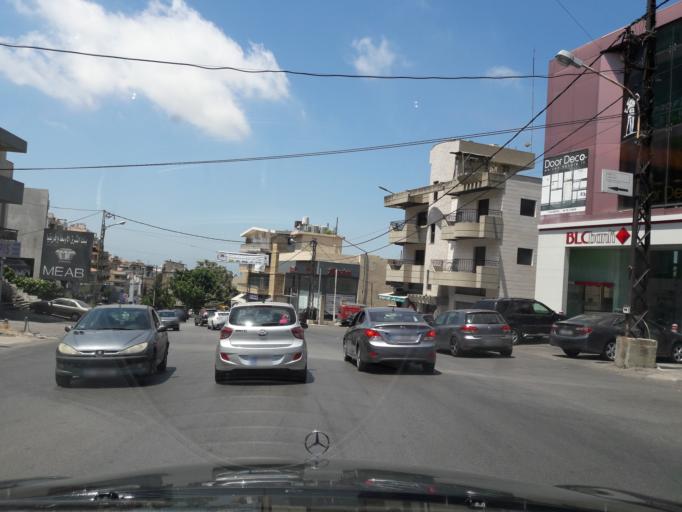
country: LB
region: Mont-Liban
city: Djounie
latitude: 33.9257
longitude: 35.6323
